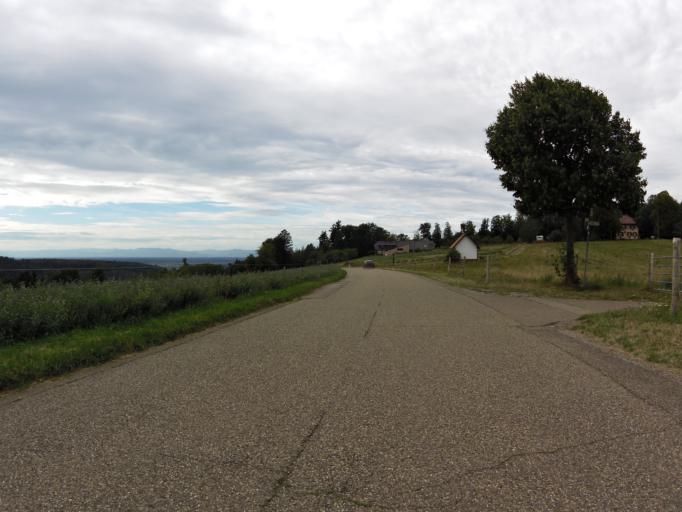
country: DE
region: Baden-Wuerttemberg
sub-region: Freiburg Region
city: Hohberg
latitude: 48.3102
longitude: 7.8959
